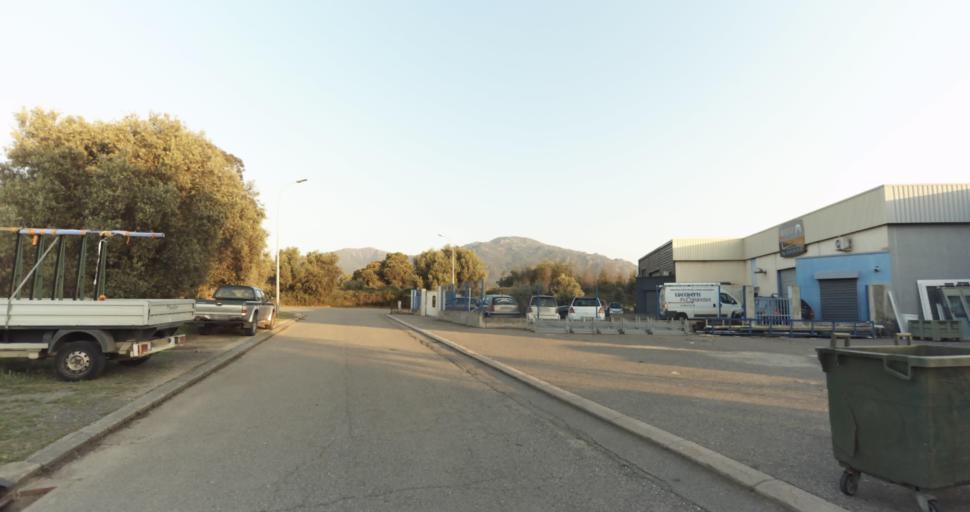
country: FR
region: Corsica
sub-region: Departement de la Haute-Corse
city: Biguglia
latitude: 42.5944
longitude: 9.4472
